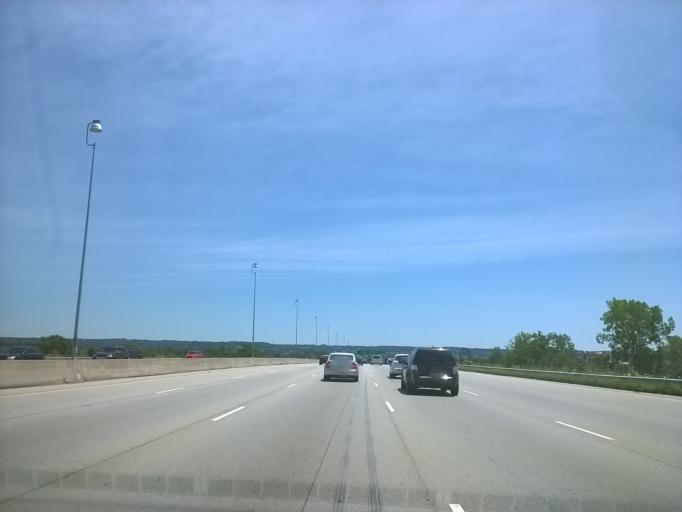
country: US
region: Ohio
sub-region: Hamilton County
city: Glendale
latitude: 39.2944
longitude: -84.4624
